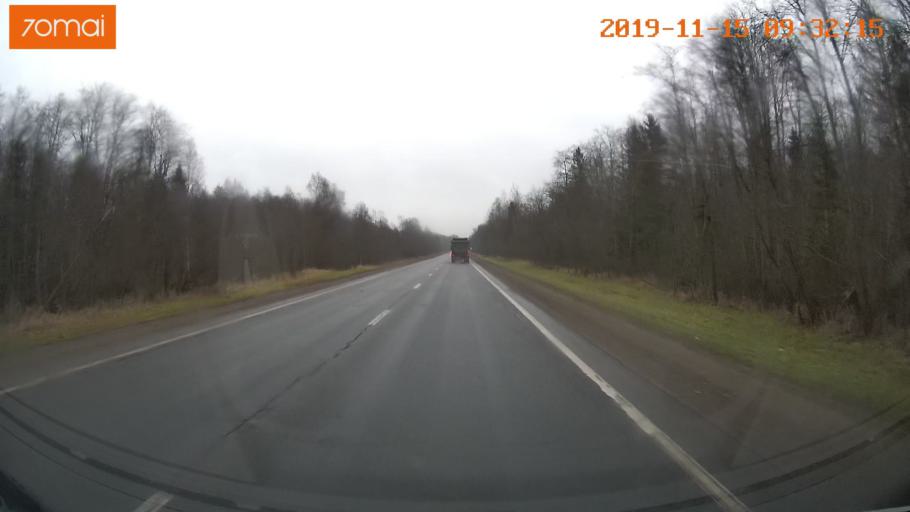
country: RU
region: Vologda
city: Sheksna
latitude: 59.2723
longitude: 38.3305
